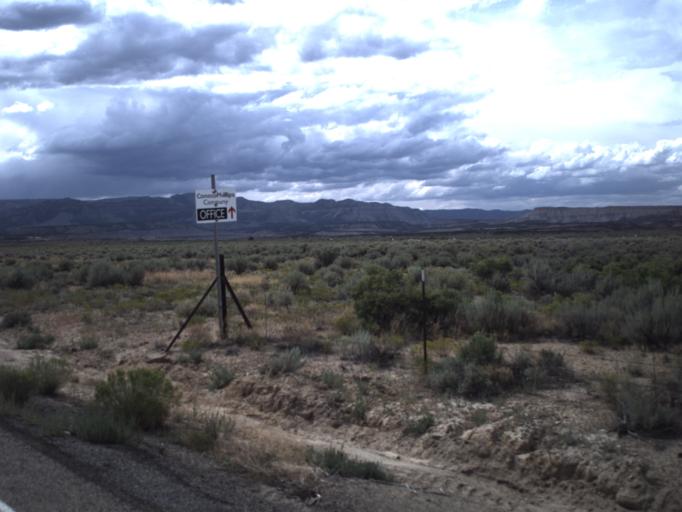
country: US
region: Utah
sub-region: Carbon County
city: Price
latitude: 39.4926
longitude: -110.8496
